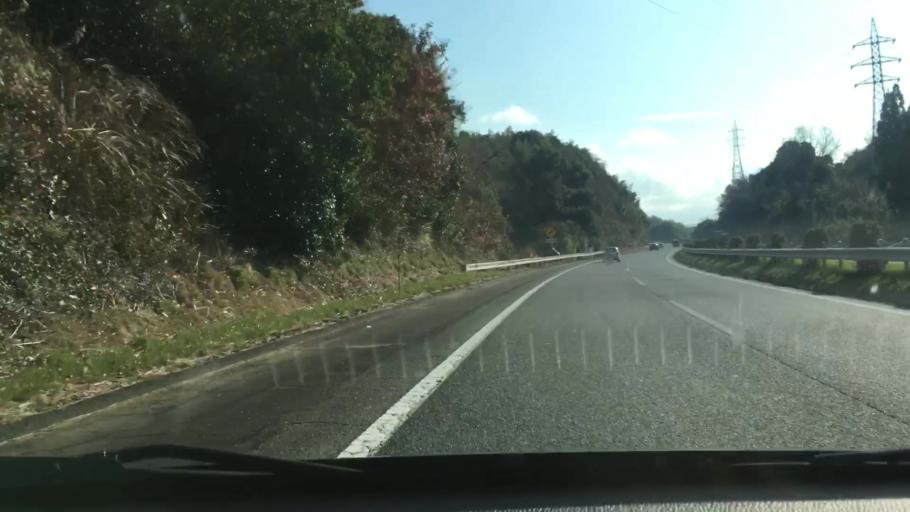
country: JP
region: Kumamoto
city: Matsubase
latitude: 32.6349
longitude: 130.7102
